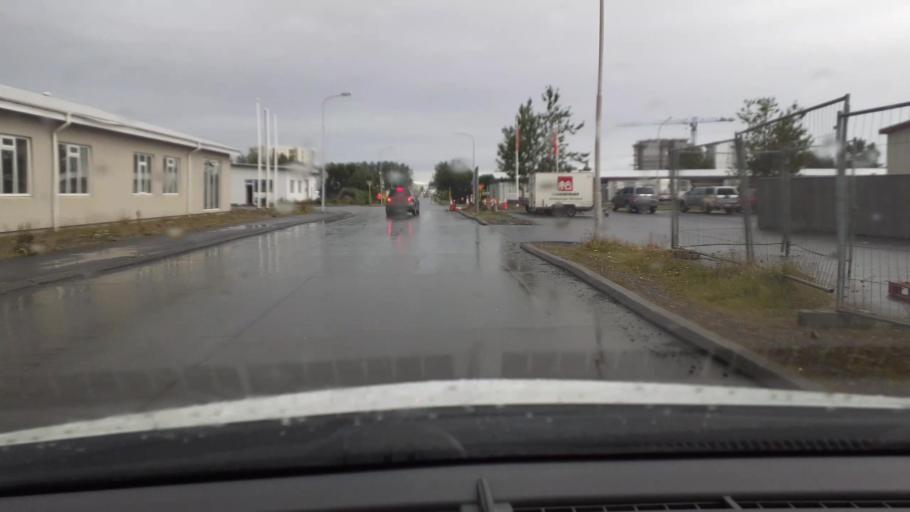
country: IS
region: West
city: Akranes
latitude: 64.3237
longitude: -22.0640
